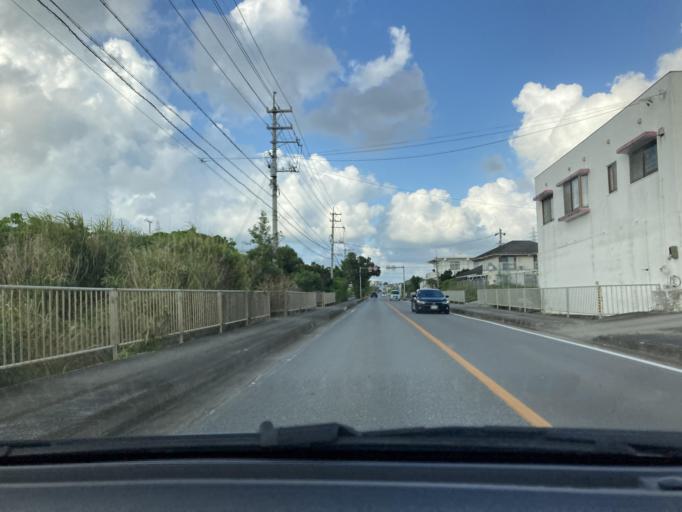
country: JP
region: Okinawa
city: Itoman
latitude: 26.1442
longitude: 127.7034
